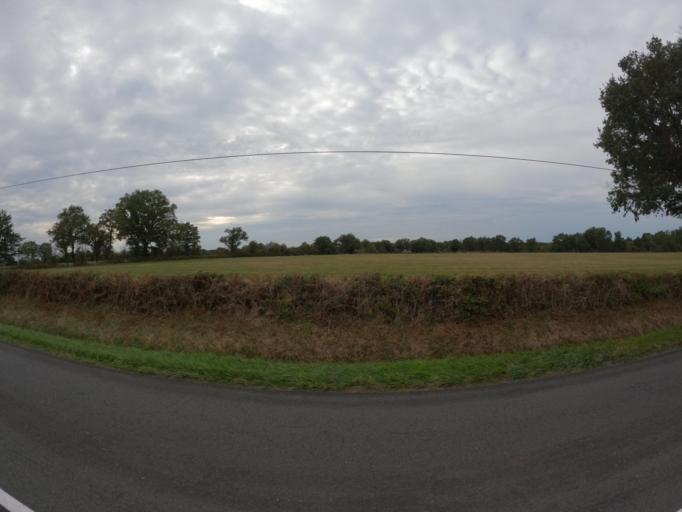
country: FR
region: Poitou-Charentes
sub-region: Departement de la Vienne
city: Saulge
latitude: 46.3437
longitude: 0.8288
